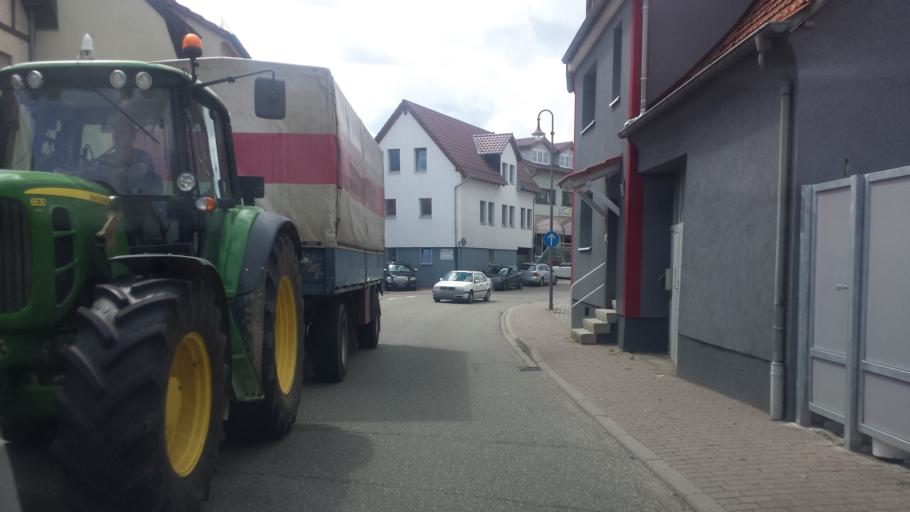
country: DE
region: Baden-Wuerttemberg
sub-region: Karlsruhe Region
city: Dielheim
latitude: 49.2826
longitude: 8.7346
